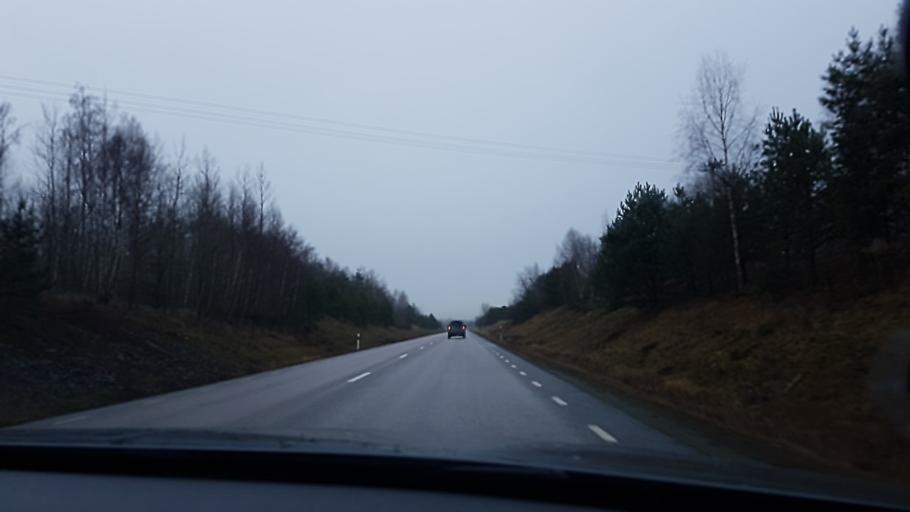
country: SE
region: Vaestra Goetaland
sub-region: Mariestads Kommun
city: Mariestad
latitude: 58.8039
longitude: 13.9742
